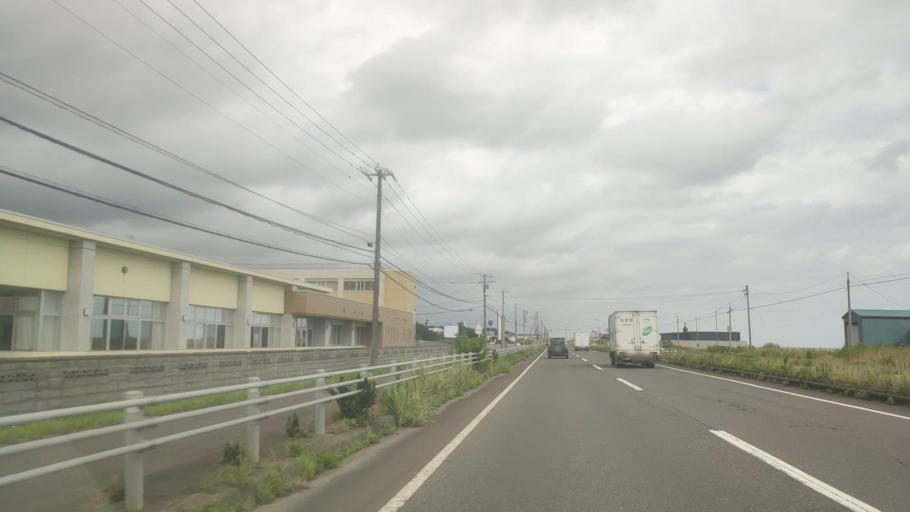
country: JP
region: Hokkaido
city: Shiraoi
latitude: 42.4706
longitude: 141.2305
